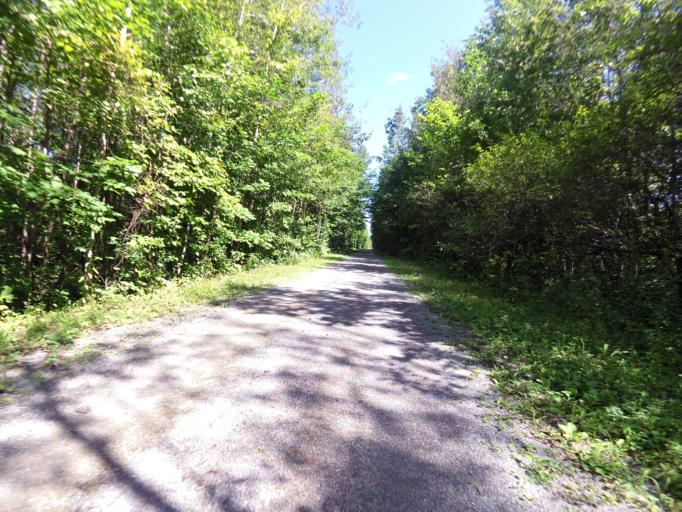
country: CA
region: Ontario
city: Ottawa
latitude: 45.2258
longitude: -75.6204
